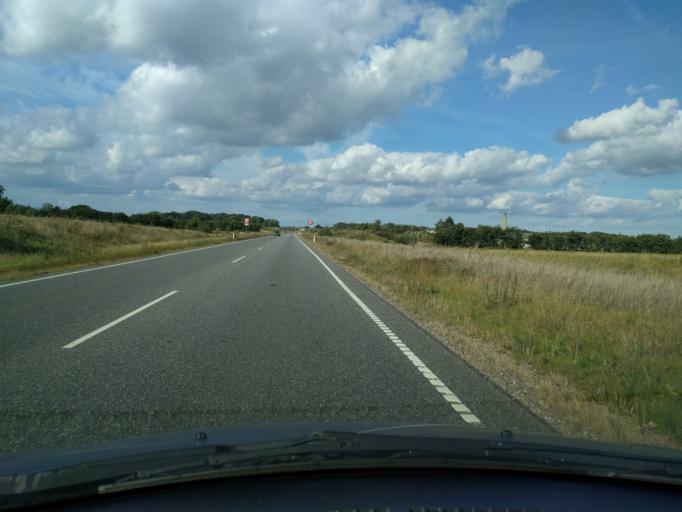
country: DK
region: South Denmark
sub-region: Odense Kommune
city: Bullerup
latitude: 55.4014
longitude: 10.4745
